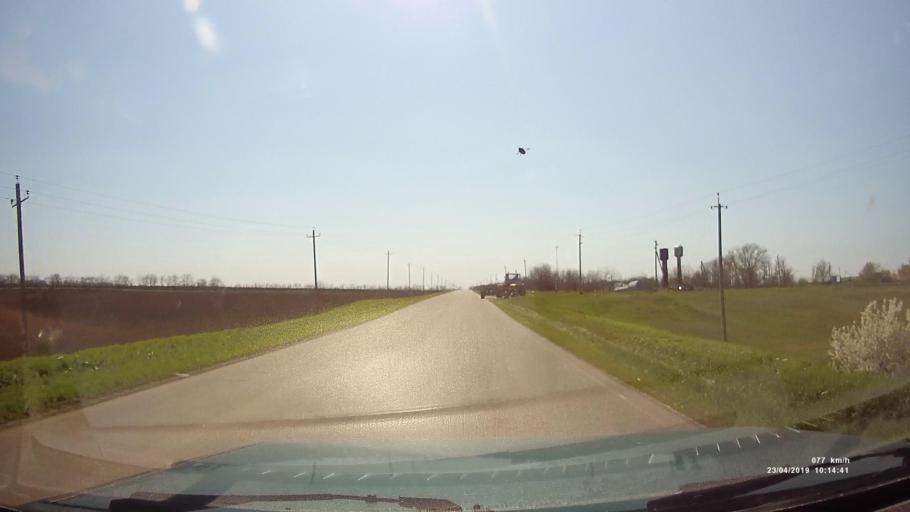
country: RU
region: Rostov
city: Sovetskoye
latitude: 46.6745
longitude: 42.3726
